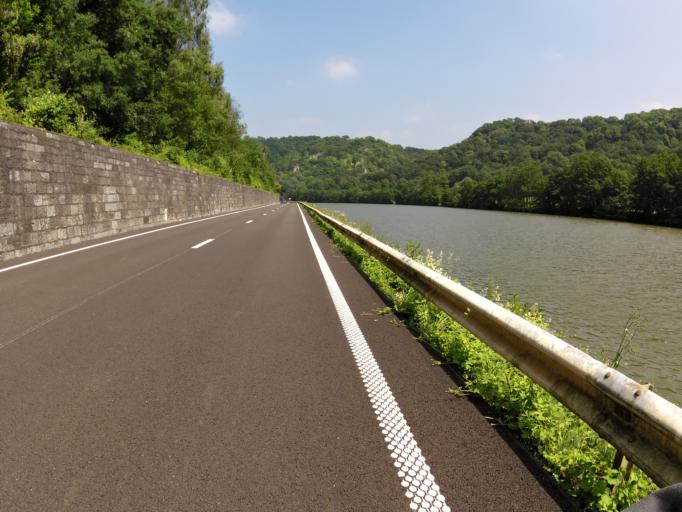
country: BE
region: Wallonia
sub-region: Province de Namur
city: Onhaye
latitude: 50.2179
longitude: 4.8807
